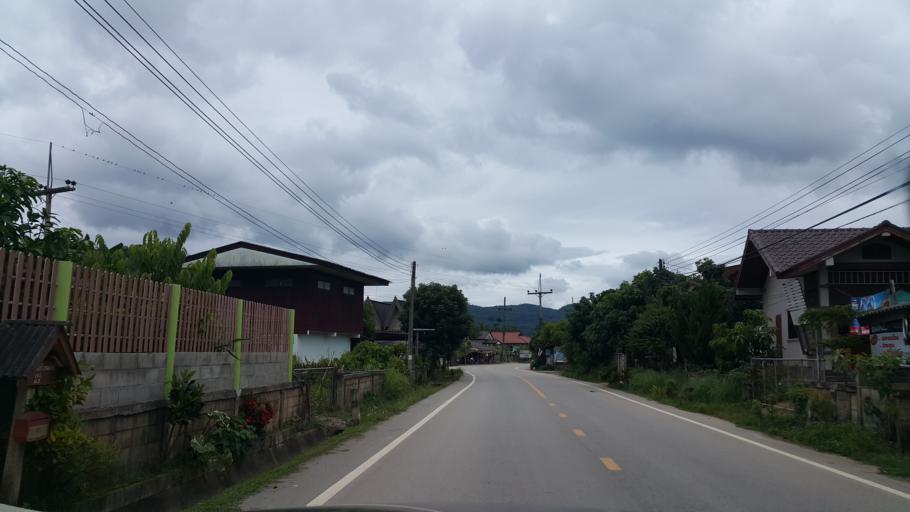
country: TH
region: Chiang Rai
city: Phaya Mengrai
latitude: 19.8944
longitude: 100.1080
